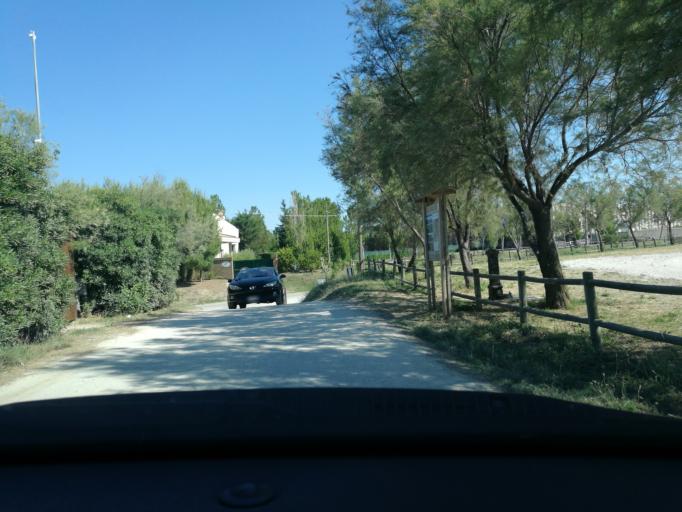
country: IT
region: Abruzzo
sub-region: Provincia di Chieti
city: Vasto
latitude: 42.1746
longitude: 14.6933
